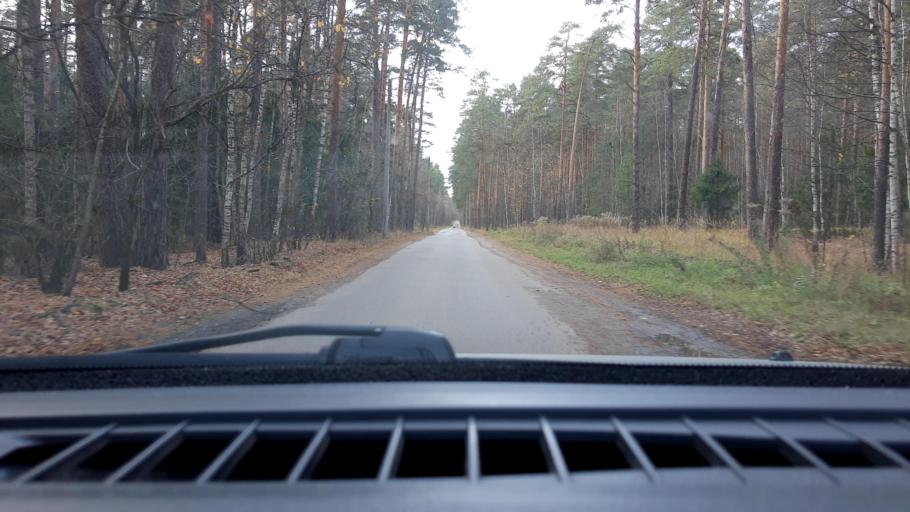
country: RU
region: Nizjnij Novgorod
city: Kstovo
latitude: 56.1680
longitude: 44.1116
